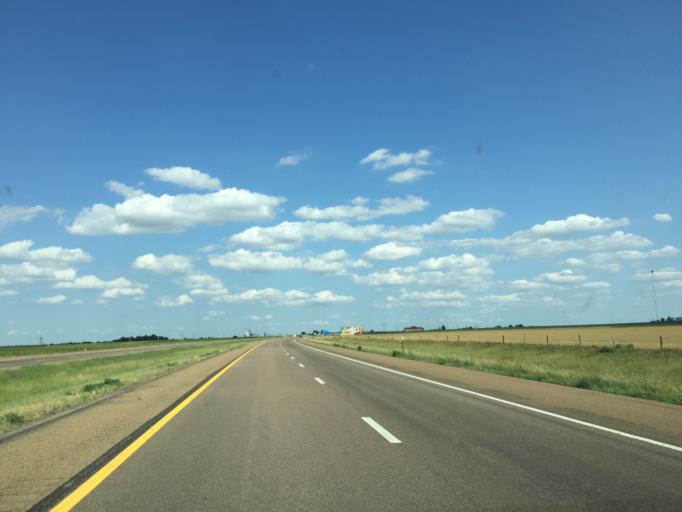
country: US
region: Kansas
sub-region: Gove County
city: Gove
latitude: 39.1115
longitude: -100.4928
